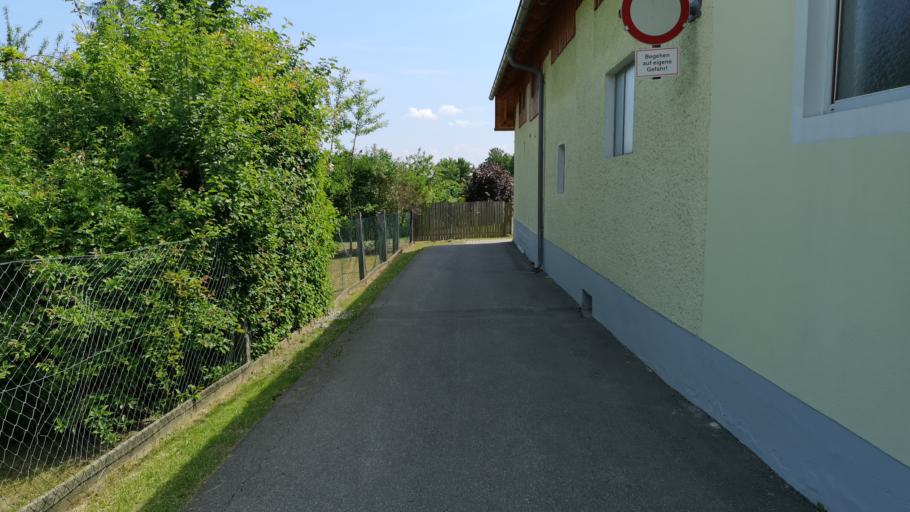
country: AT
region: Styria
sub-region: Politischer Bezirk Graz-Umgebung
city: Seiersberg
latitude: 47.0260
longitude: 15.3924
